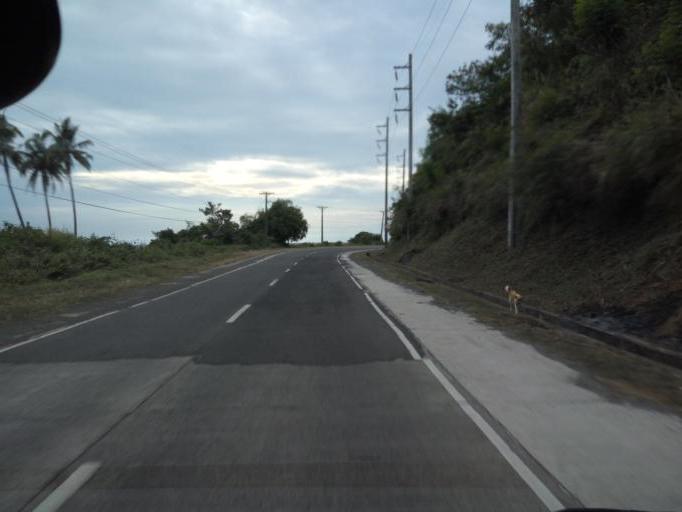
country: PH
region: Cagayan Valley
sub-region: Province of Cagayan
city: Casambalangan
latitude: 18.3964
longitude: 122.1270
